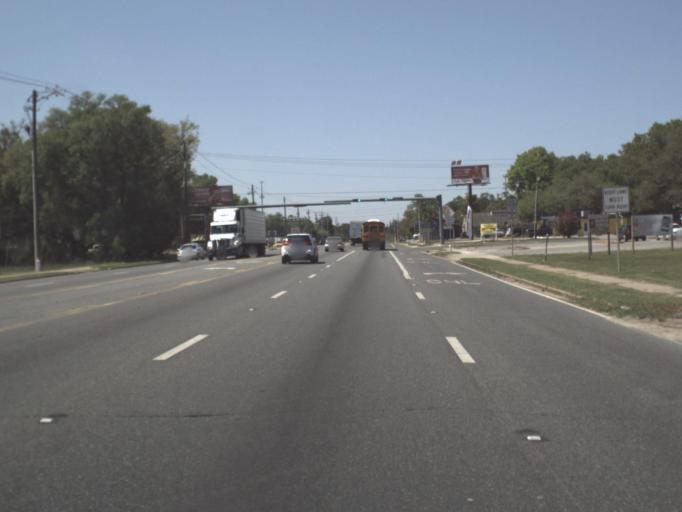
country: US
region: Florida
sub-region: Escambia County
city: West Pensacola
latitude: 30.4399
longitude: -87.2818
